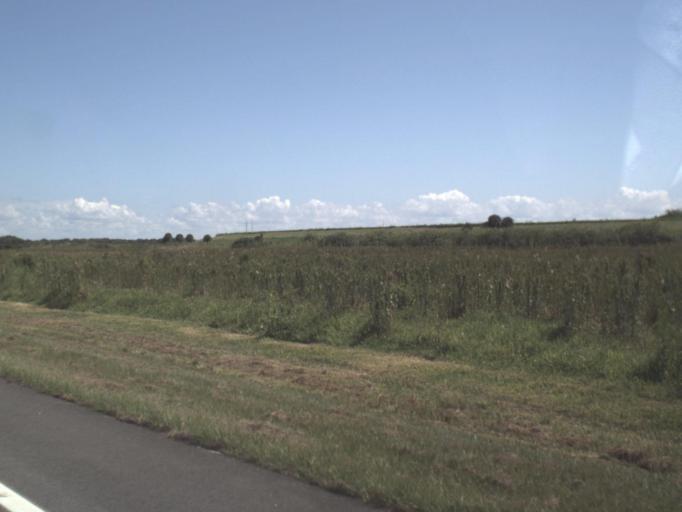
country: US
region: Florida
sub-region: Glades County
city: Moore Haven
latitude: 26.9764
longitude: -81.1133
